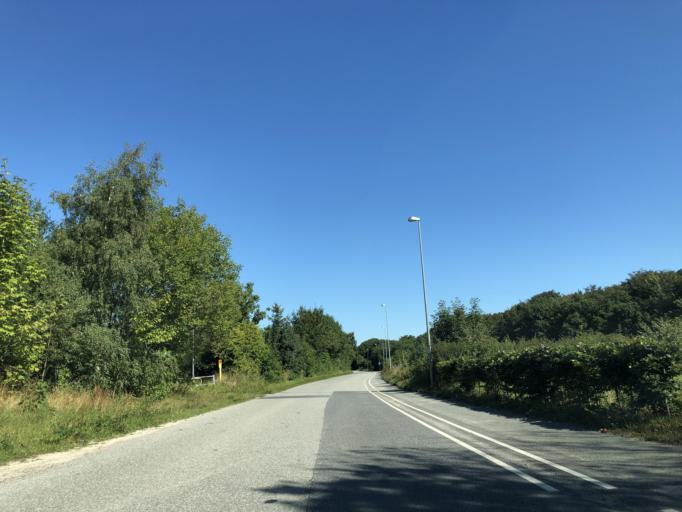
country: DK
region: North Denmark
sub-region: Mariagerfjord Kommune
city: Hobro
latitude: 56.6396
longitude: 9.7729
